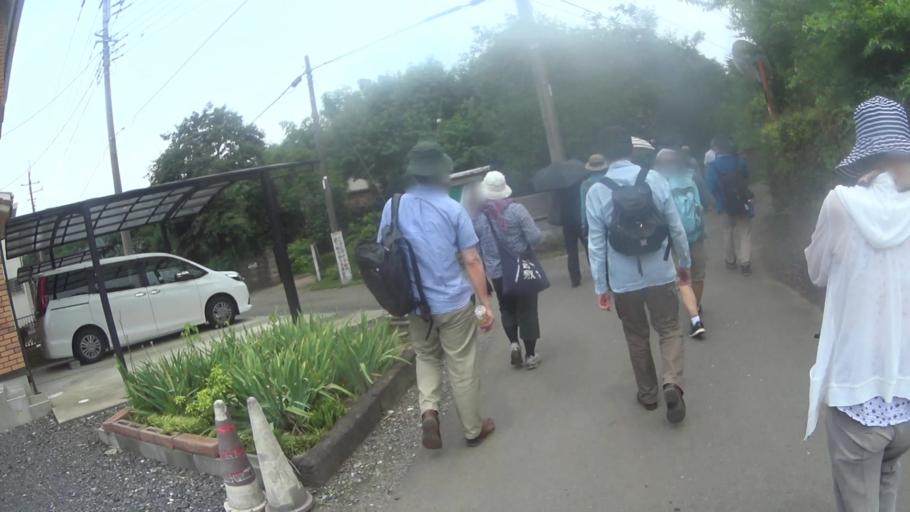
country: JP
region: Saitama
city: Ageoshimo
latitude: 35.9370
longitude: 139.5678
